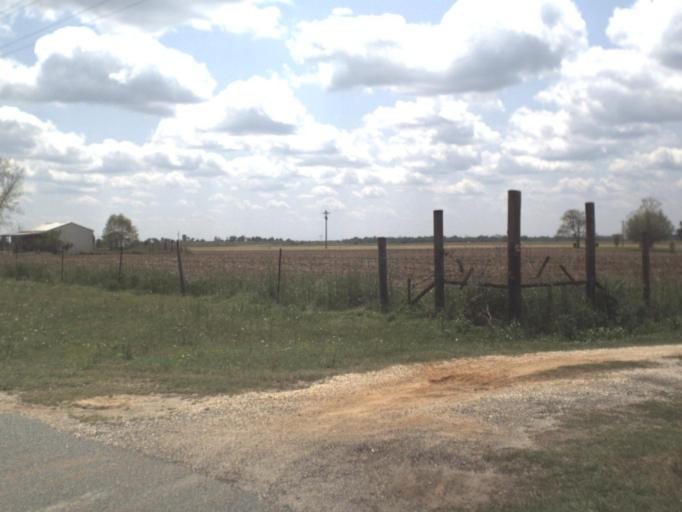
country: US
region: Alabama
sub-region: Escambia County
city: Atmore
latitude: 30.9436
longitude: -87.4877
